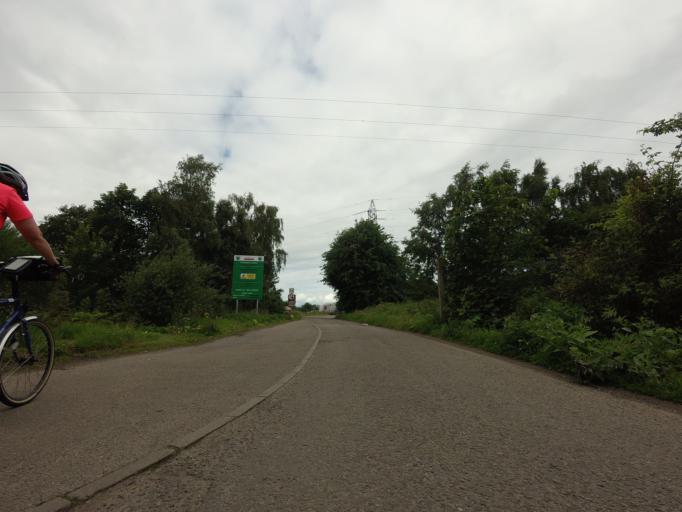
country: GB
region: Scotland
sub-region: Moray
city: Forres
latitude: 57.6159
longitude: -3.6299
